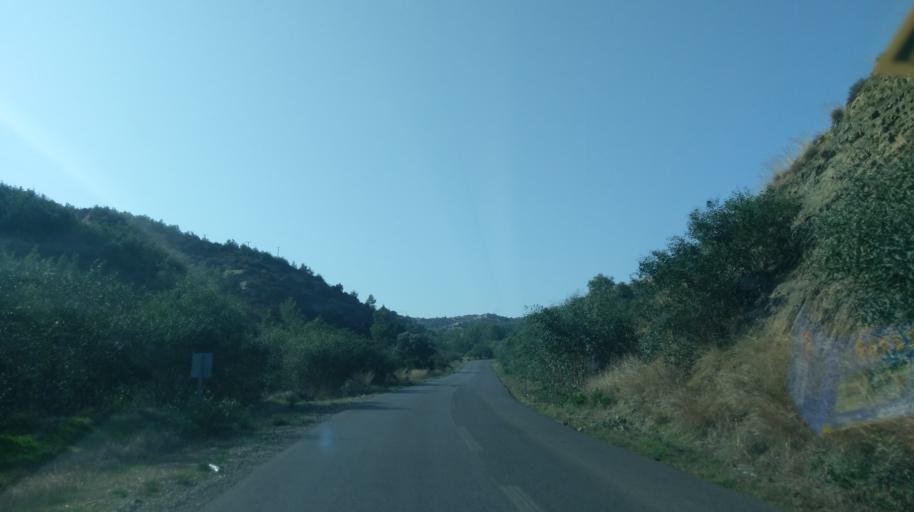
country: CY
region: Lefkosia
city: Lefka
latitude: 35.1521
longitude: 32.7796
